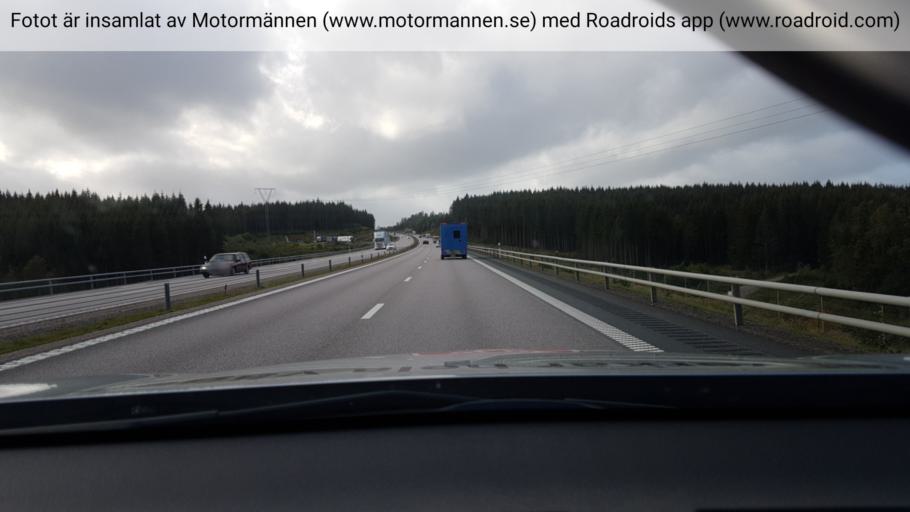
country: SE
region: Vaestra Goetaland
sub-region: Ulricehamns Kommun
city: Ulricehamn
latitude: 57.8159
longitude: 13.3509
